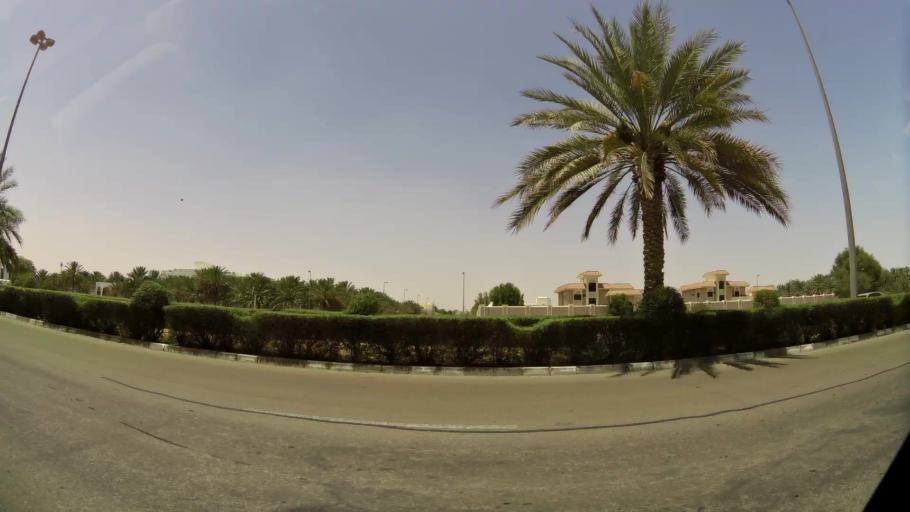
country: OM
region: Al Buraimi
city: Al Buraymi
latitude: 24.2591
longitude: 55.7163
